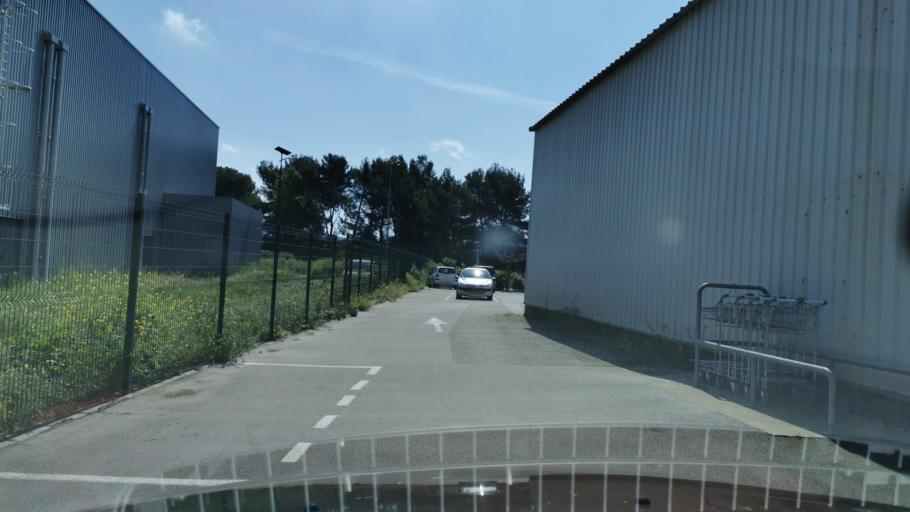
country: FR
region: Languedoc-Roussillon
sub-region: Departement de l'Aude
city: Narbonne
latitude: 43.1760
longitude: 3.0299
